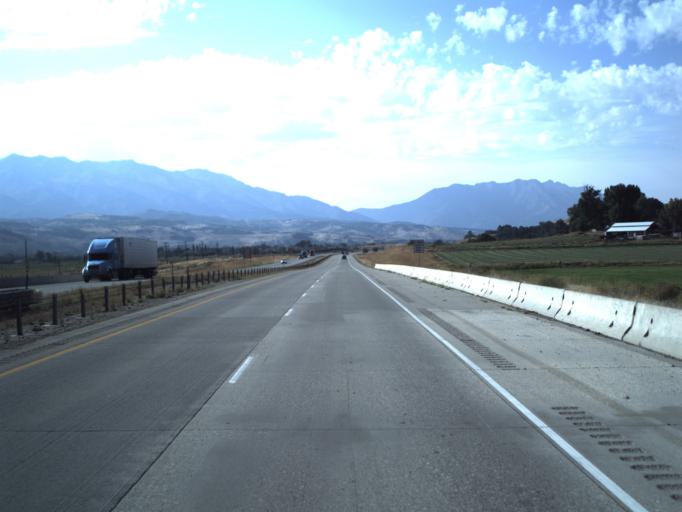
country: US
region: Utah
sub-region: Morgan County
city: Morgan
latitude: 41.0550
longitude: -111.6923
